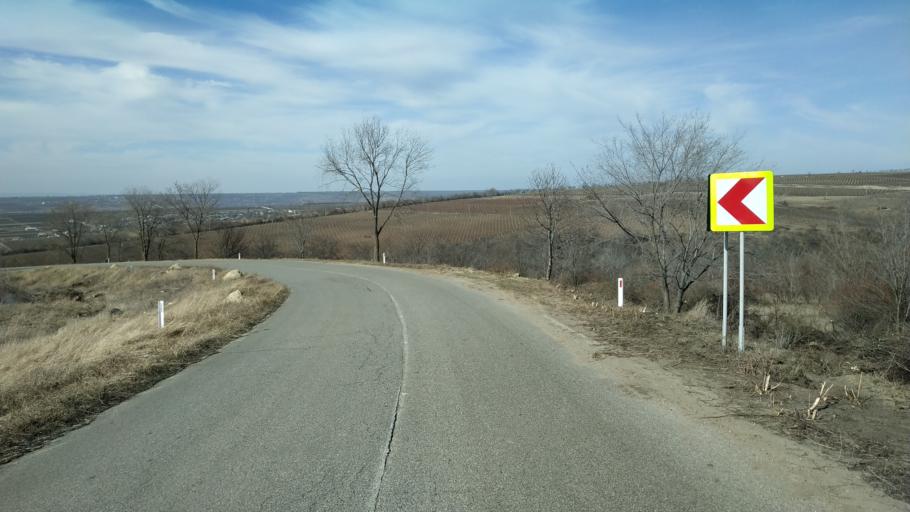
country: MD
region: Nisporeni
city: Nisporeni
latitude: 46.9567
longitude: 28.2350
